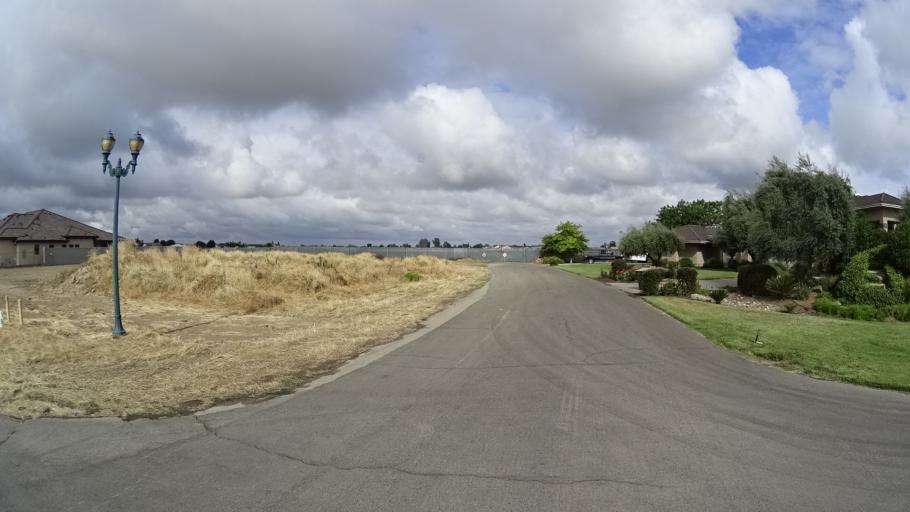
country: US
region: California
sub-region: Kings County
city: Lucerne
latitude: 36.3517
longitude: -119.6774
